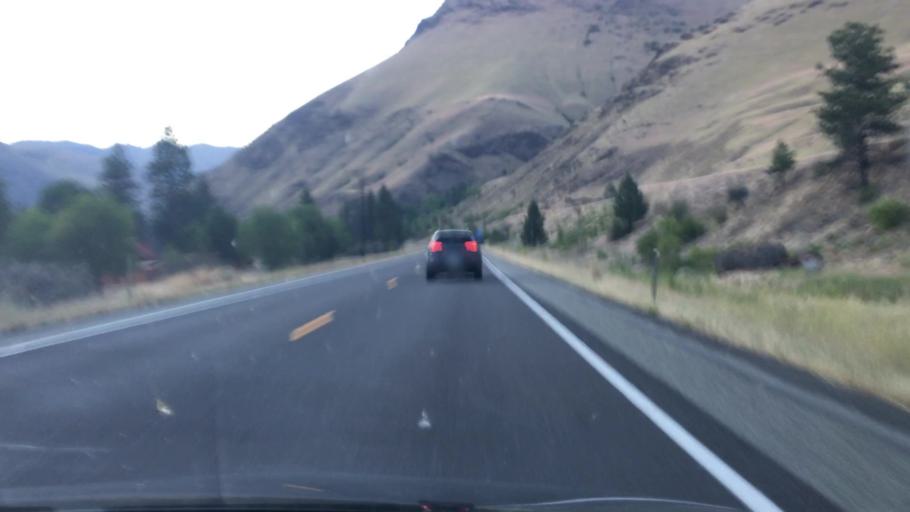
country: US
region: Idaho
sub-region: Valley County
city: McCall
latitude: 45.3358
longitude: -116.3475
